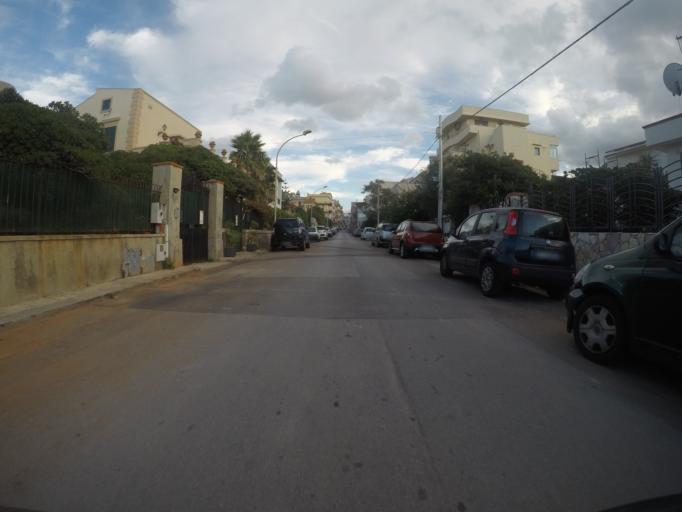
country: IT
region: Sicily
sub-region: Palermo
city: Isola delle Femmine
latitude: 38.2014
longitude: 13.2770
